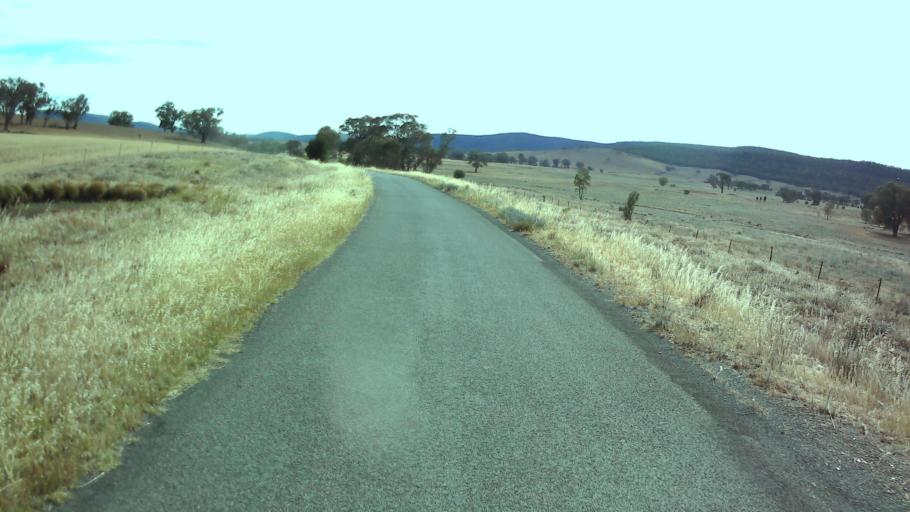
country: AU
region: New South Wales
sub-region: Weddin
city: Grenfell
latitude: -33.8277
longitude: 148.2840
